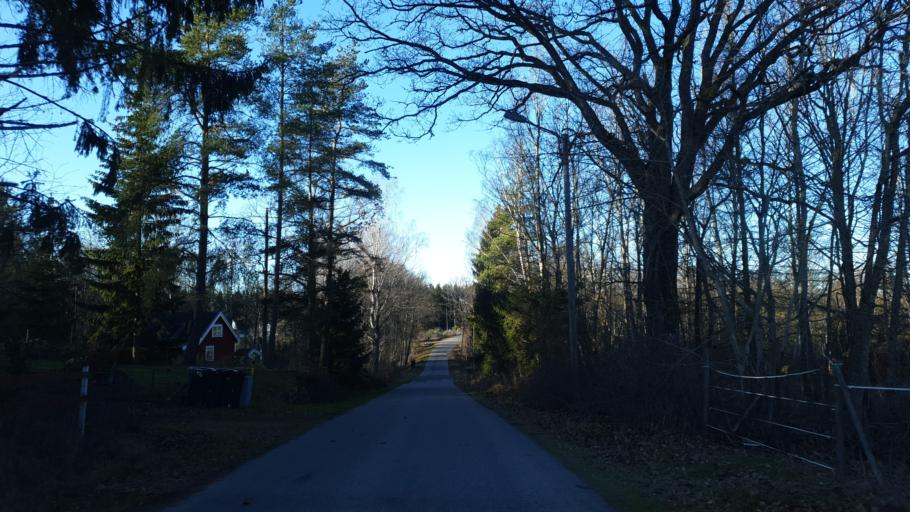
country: SE
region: Blekinge
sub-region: Karlskrona Kommun
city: Nattraby
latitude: 56.2671
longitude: 15.4691
